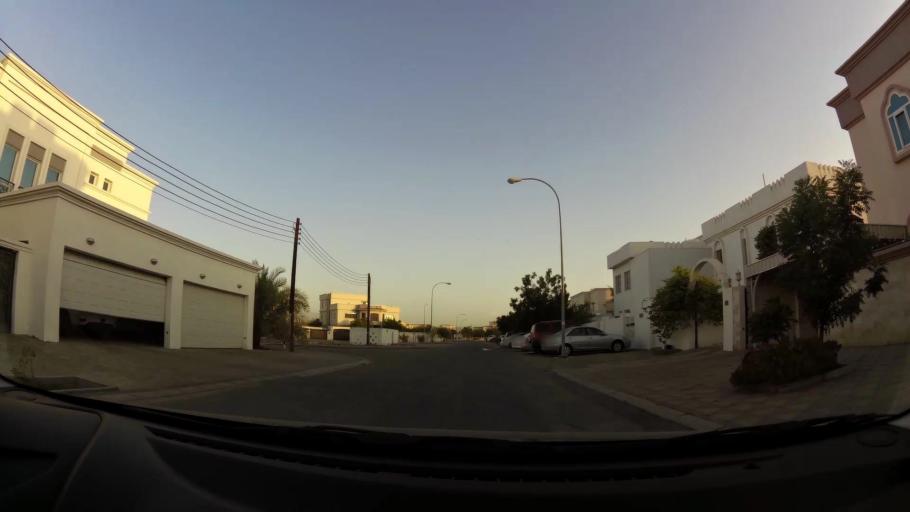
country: OM
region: Muhafazat Masqat
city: As Sib al Jadidah
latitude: 23.6137
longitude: 58.2032
